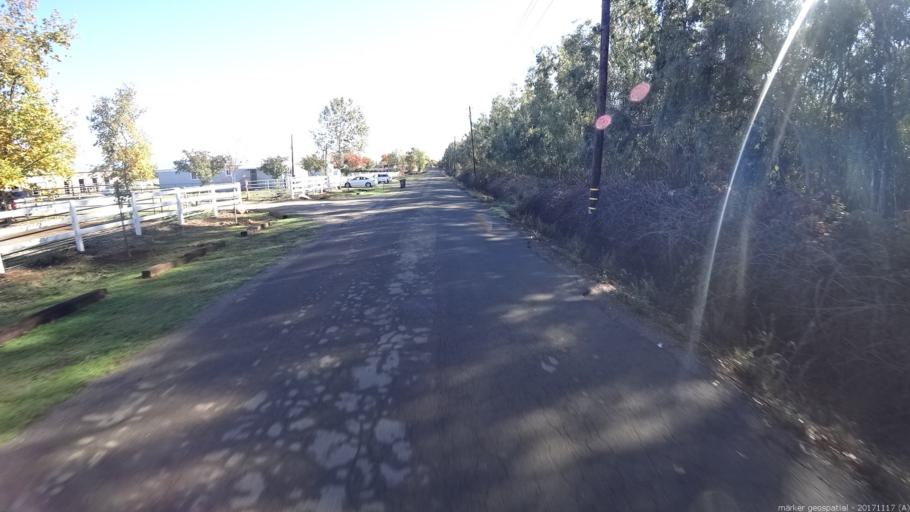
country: US
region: California
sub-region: Shasta County
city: Anderson
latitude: 40.4355
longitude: -122.2610
